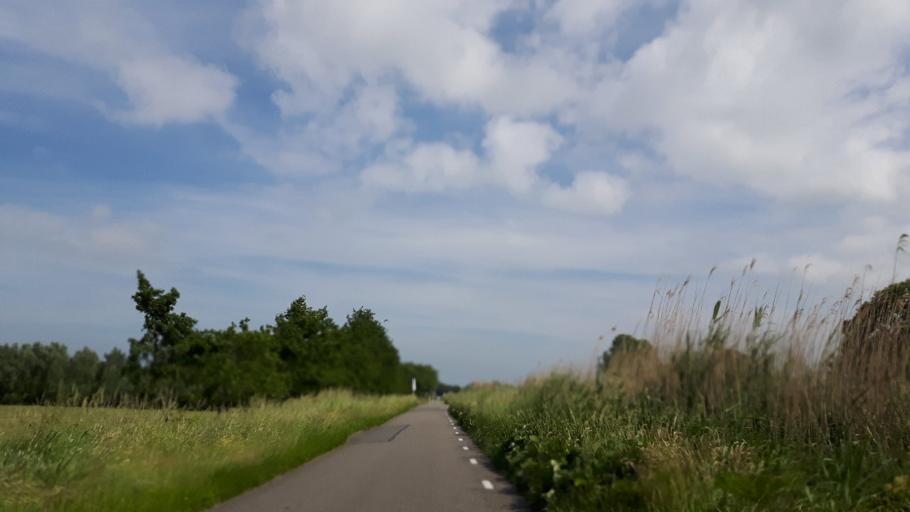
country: NL
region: Utrecht
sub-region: Gemeente De Ronde Venen
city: Mijdrecht
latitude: 52.1772
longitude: 4.8597
